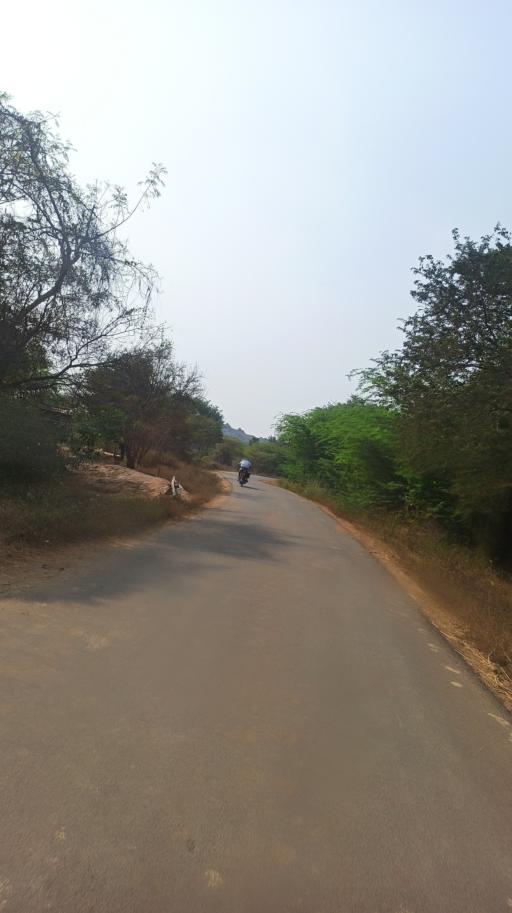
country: IN
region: Tamil Nadu
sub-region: Tiruvannamalai
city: Desur
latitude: 12.4374
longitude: 79.3906
